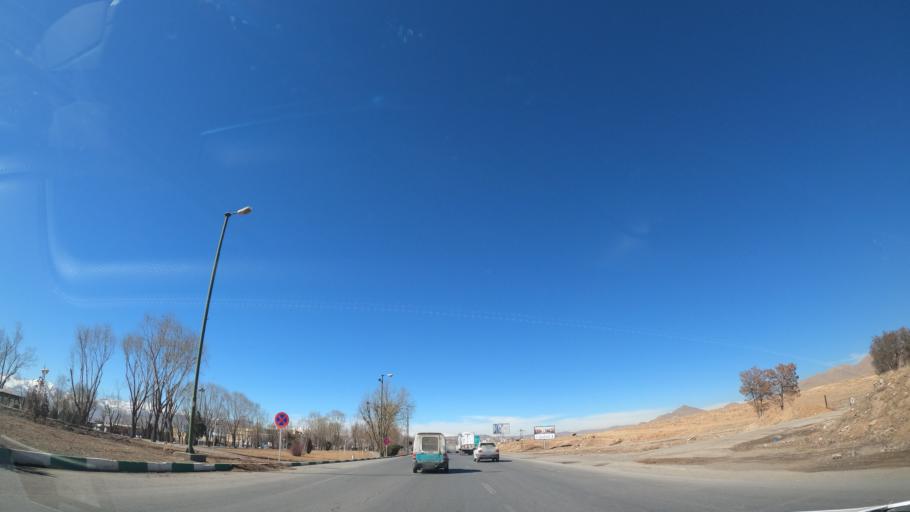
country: IR
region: Chahar Mahall va Bakhtiari
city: Shahrekord
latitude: 32.3074
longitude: 50.9057
